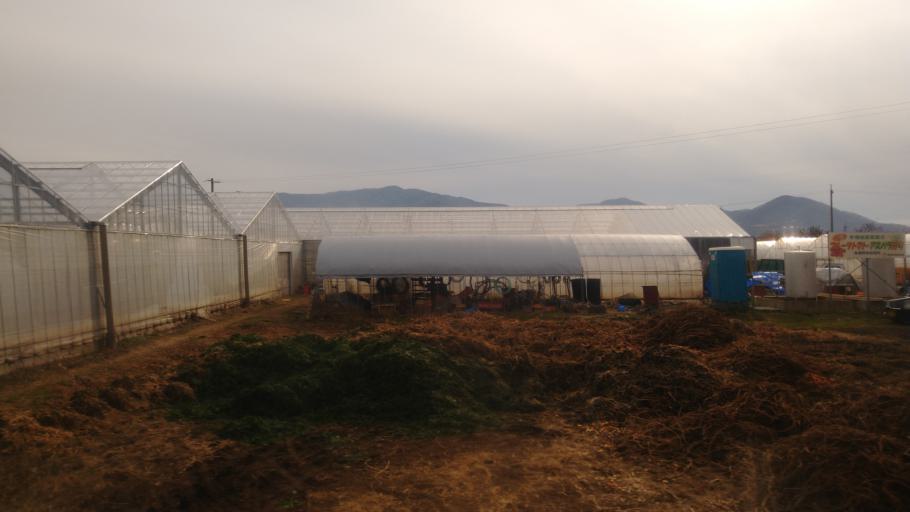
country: JP
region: Nagano
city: Nagano-shi
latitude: 36.5640
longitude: 138.1238
